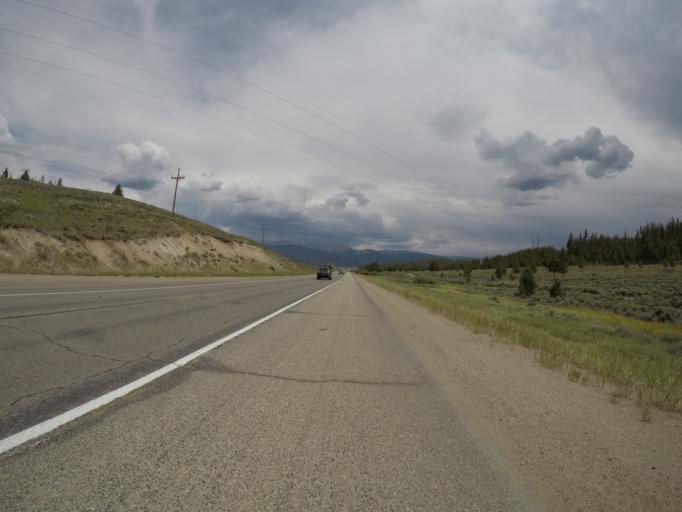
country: US
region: Colorado
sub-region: Grand County
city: Fraser
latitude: 39.9956
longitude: -105.8771
